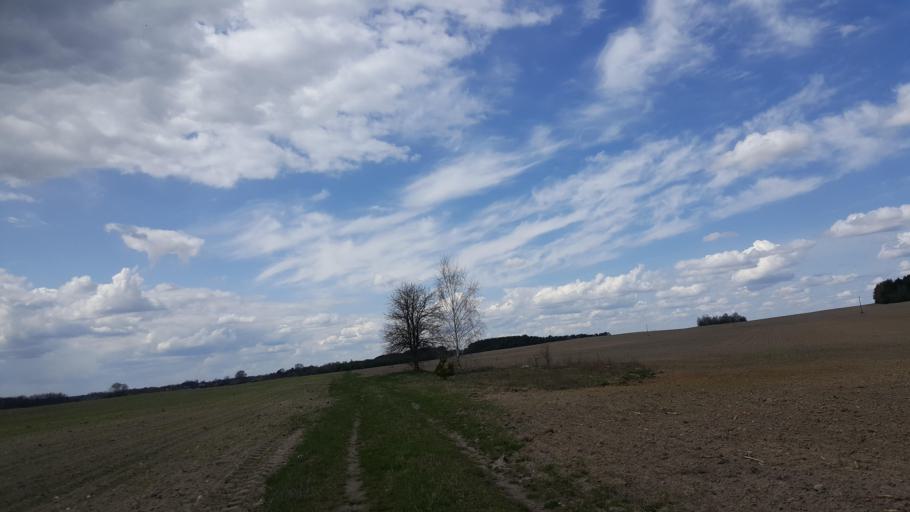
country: BY
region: Brest
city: Kamyanyets
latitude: 52.3515
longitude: 23.7240
